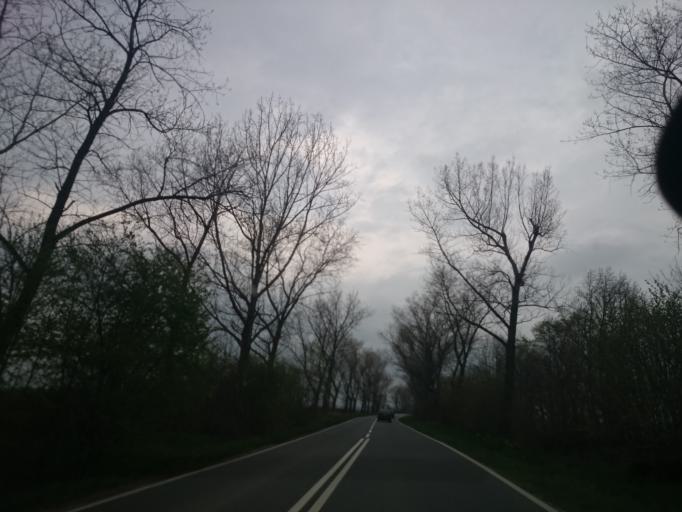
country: PL
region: Lower Silesian Voivodeship
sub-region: Powiat zabkowicki
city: Kamieniec Zabkowicki
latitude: 50.5505
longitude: 16.8587
